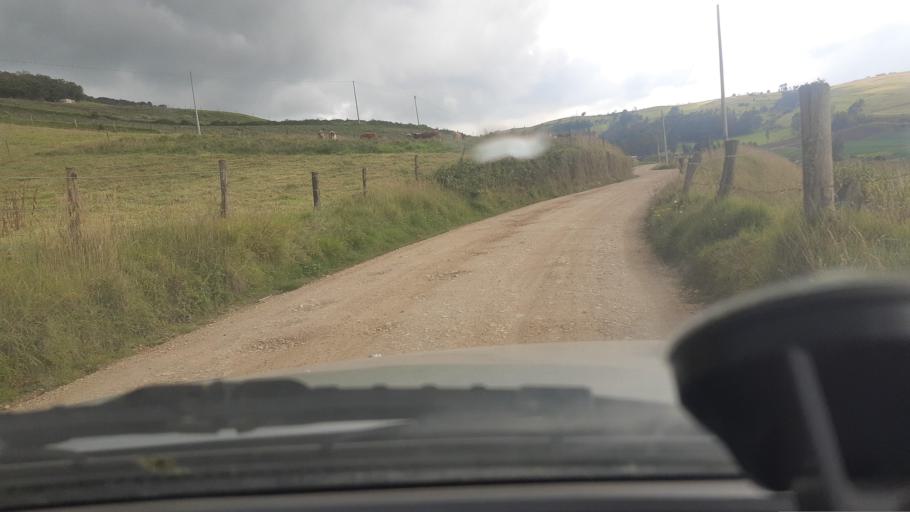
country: CO
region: Cundinamarca
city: Suesca
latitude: 5.1653
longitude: -73.7722
